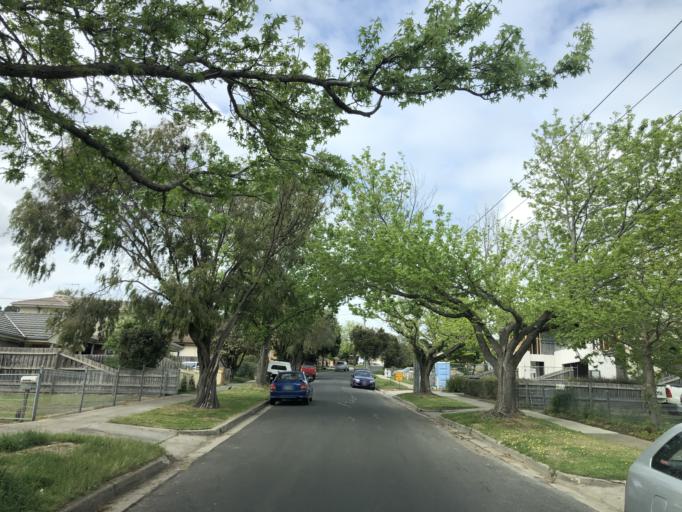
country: AU
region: Victoria
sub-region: Monash
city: Chadstone
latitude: -37.8790
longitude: 145.0951
